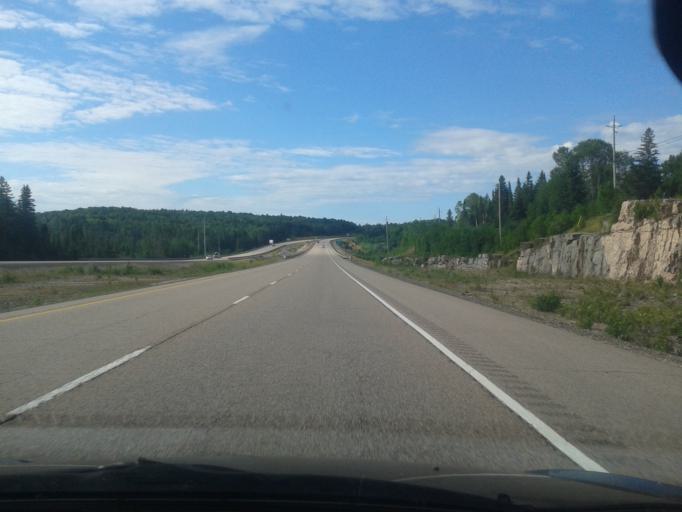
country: CA
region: Ontario
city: South River
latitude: 45.9183
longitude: -79.3654
